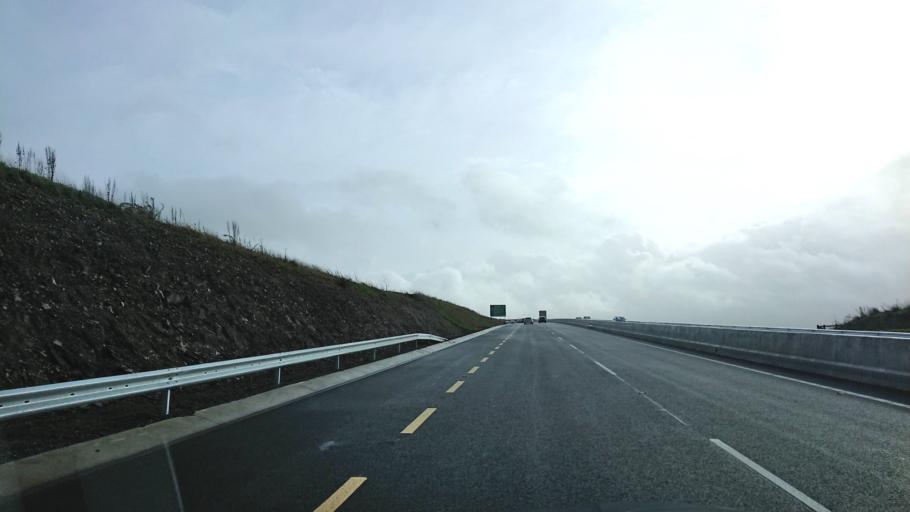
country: IE
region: Leinster
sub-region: Loch Garman
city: New Ross
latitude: 52.3595
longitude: -7.0069
